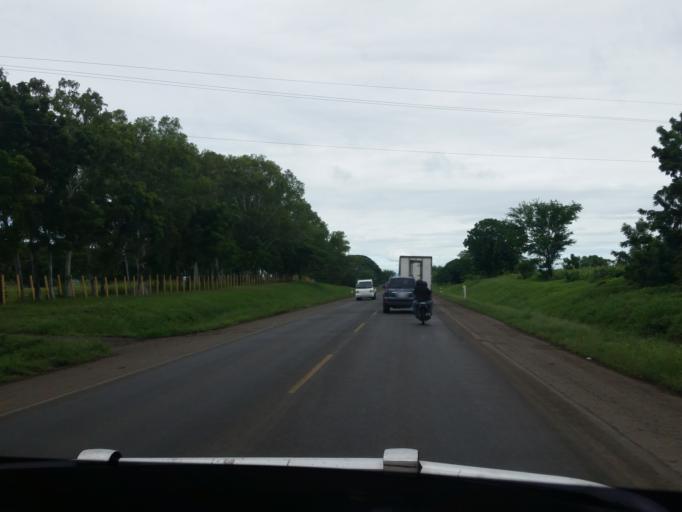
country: NI
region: Managua
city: Tipitapa
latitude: 12.2297
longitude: -86.0942
